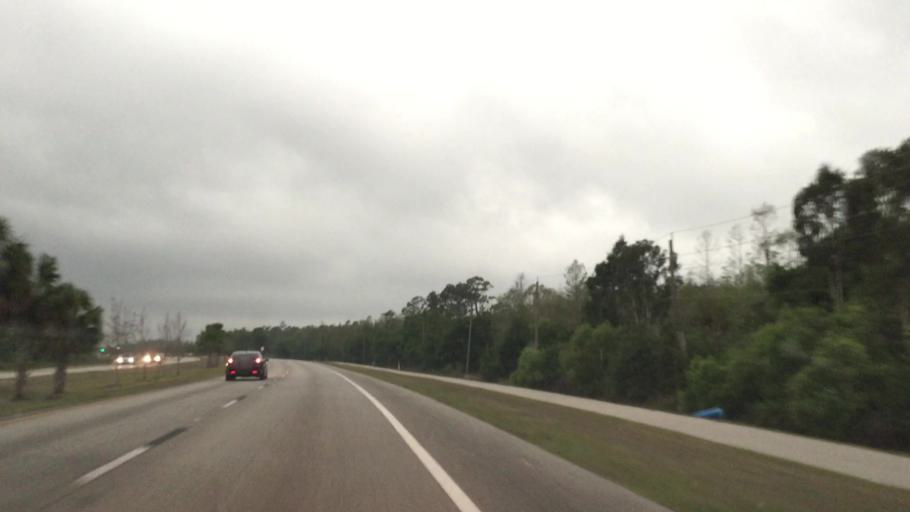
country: US
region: Florida
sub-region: Lee County
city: Fort Myers
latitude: 26.5822
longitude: -81.8226
